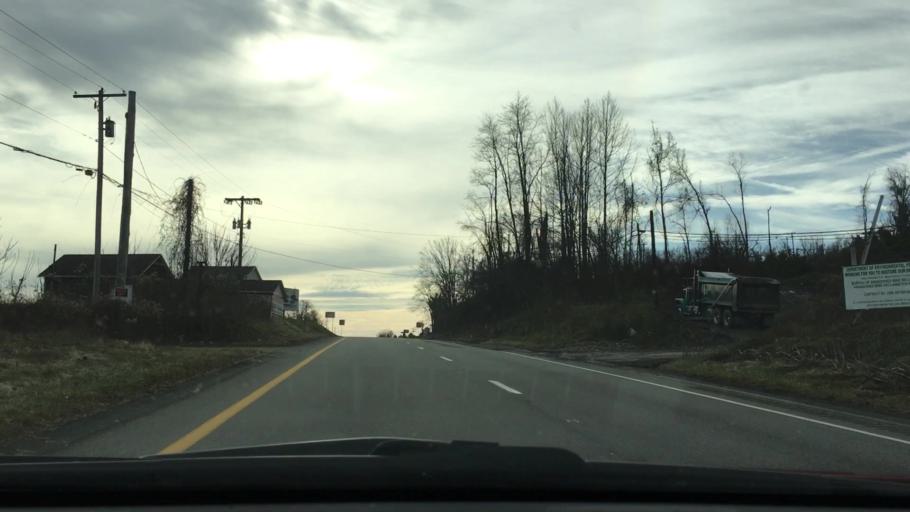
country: US
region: Pennsylvania
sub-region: Fayette County
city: Oliver
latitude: 39.9402
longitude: -79.7319
